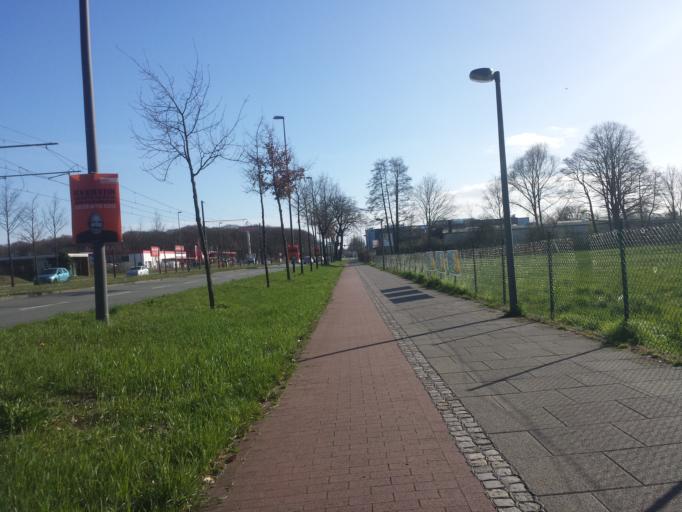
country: DE
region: Lower Saxony
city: Oyten
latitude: 53.0559
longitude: 8.9628
